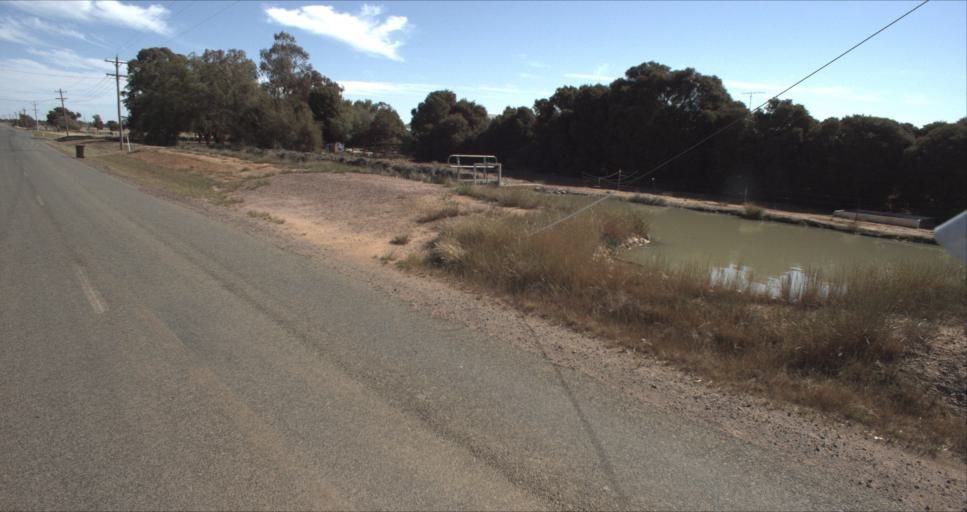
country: AU
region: New South Wales
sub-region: Leeton
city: Leeton
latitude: -34.5638
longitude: 146.3831
